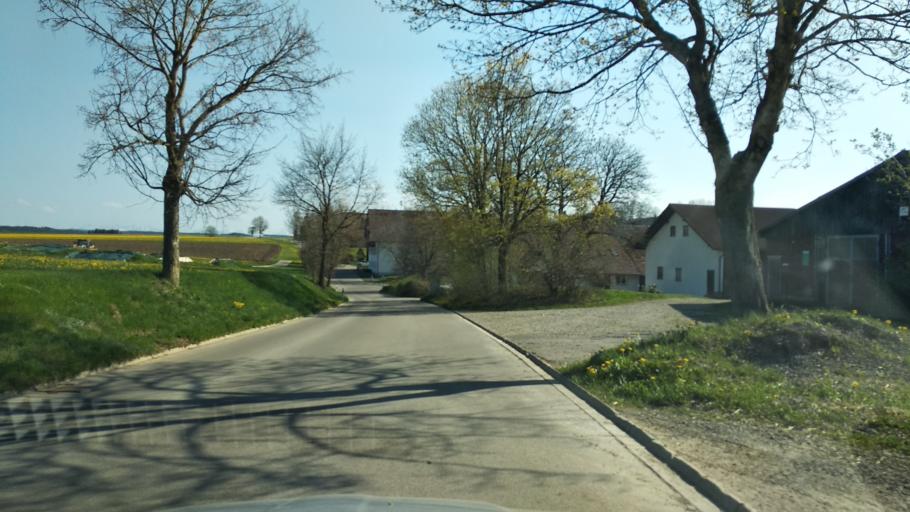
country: DE
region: Bavaria
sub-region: Swabia
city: Wald
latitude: 47.9821
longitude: 10.3101
